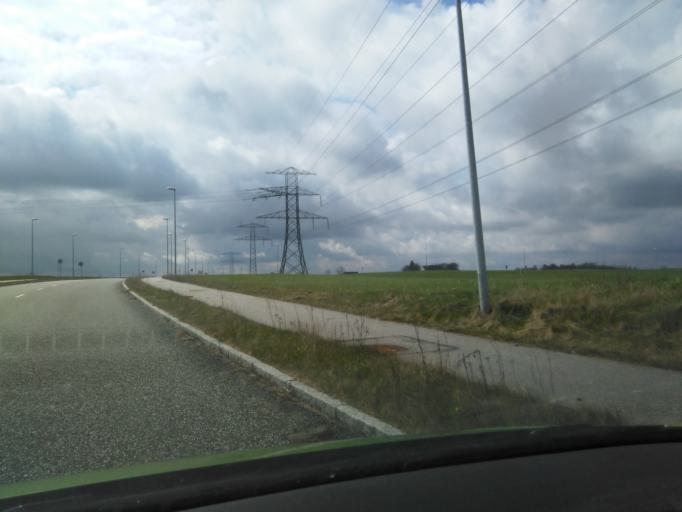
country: DK
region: Central Jutland
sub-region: Arhus Kommune
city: Framlev
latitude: 56.1571
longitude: 10.0597
